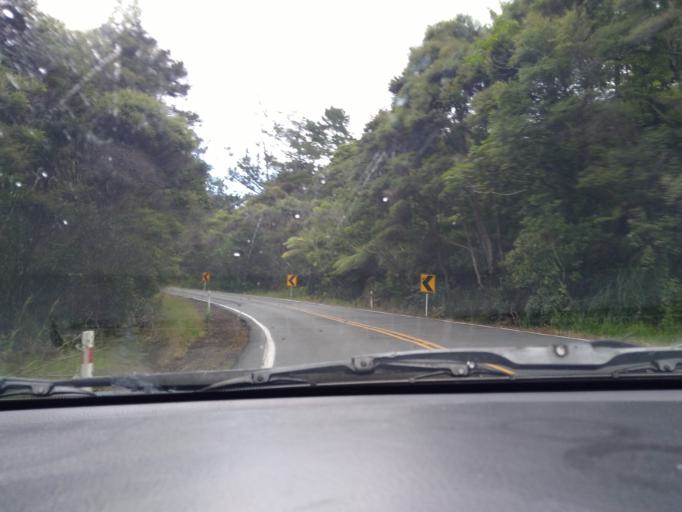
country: NZ
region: Auckland
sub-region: Auckland
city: Titirangi
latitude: -37.0003
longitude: 174.5877
